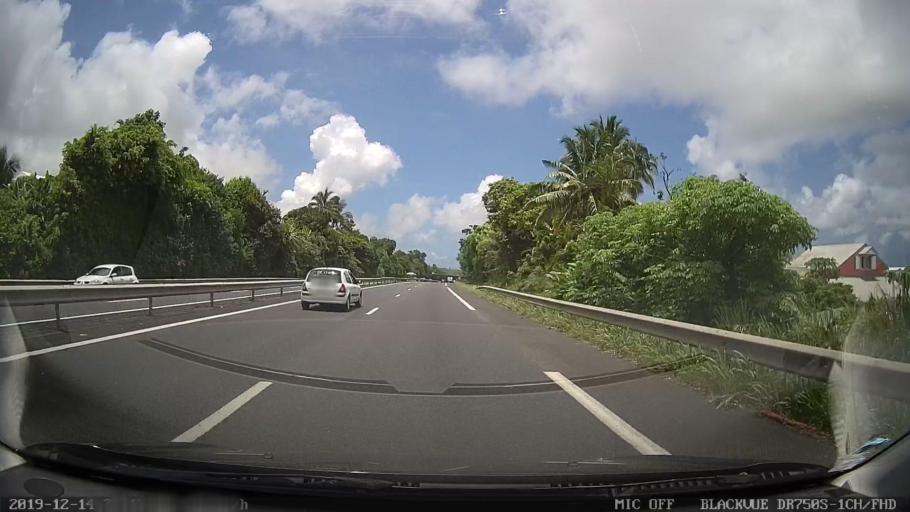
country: RE
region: Reunion
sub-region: Reunion
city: Saint-Andre
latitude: -20.9374
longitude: 55.6409
